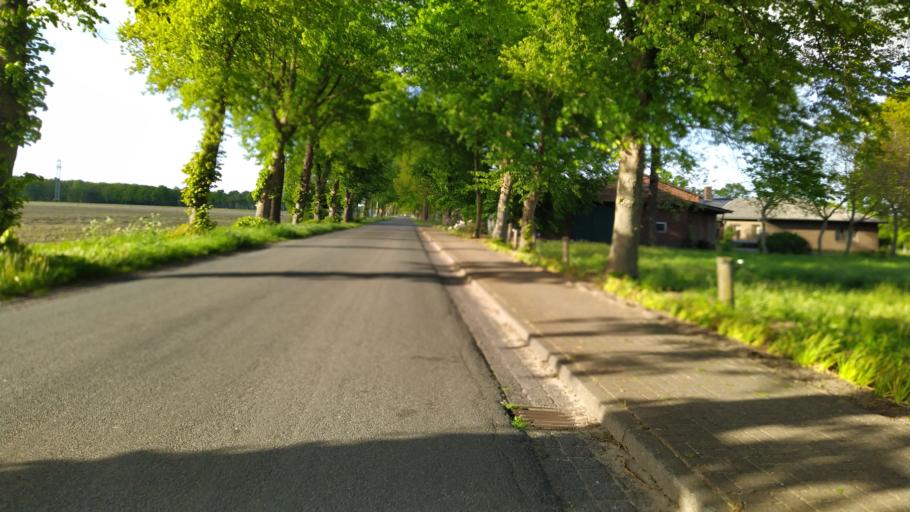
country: DE
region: Lower Saxony
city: Farven
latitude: 53.4166
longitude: 9.3327
